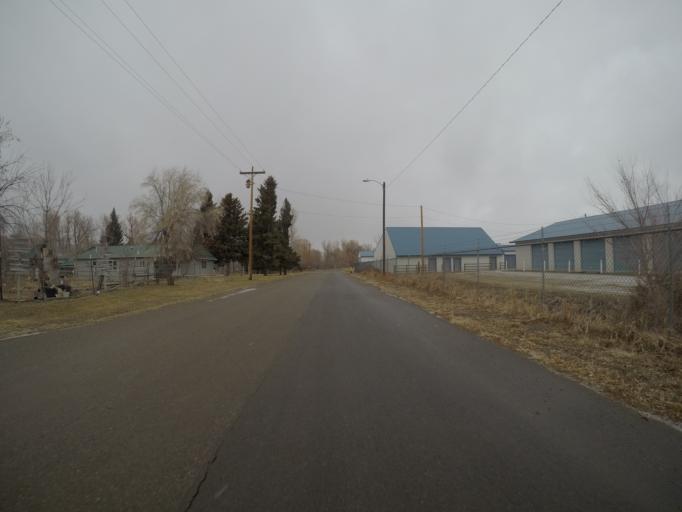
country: US
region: Montana
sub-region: Stillwater County
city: Absarokee
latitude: 45.5251
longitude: -109.4385
